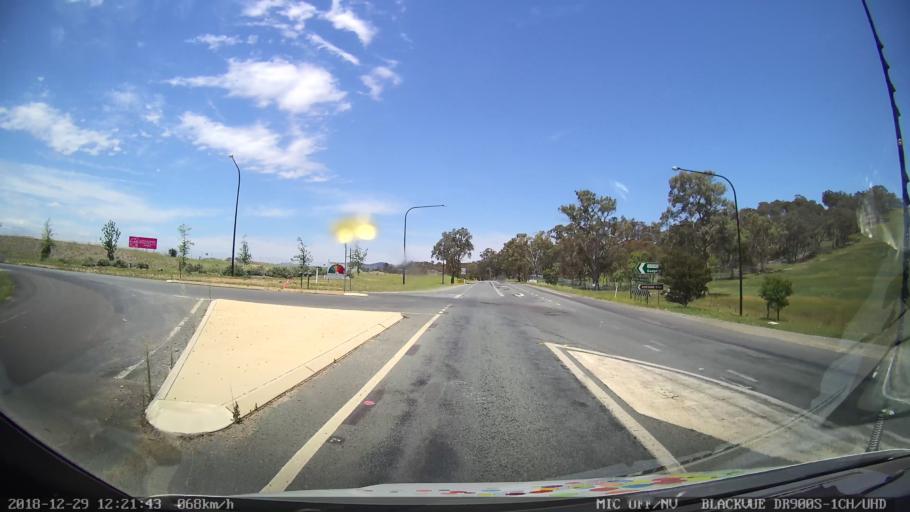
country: AU
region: New South Wales
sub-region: Queanbeyan
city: Queanbeyan
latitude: -35.4166
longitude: 149.2222
